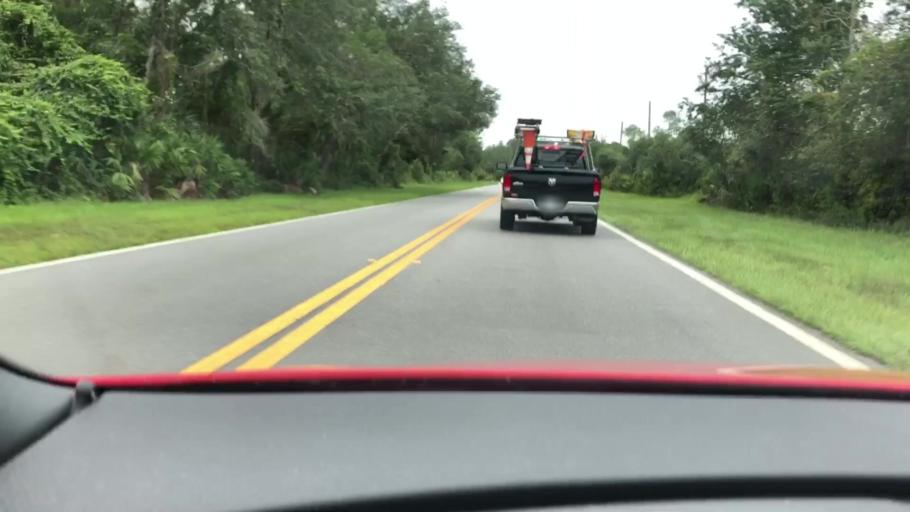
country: US
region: Florida
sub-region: Flagler County
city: Palm Coast
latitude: 29.5396
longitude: -81.2072
